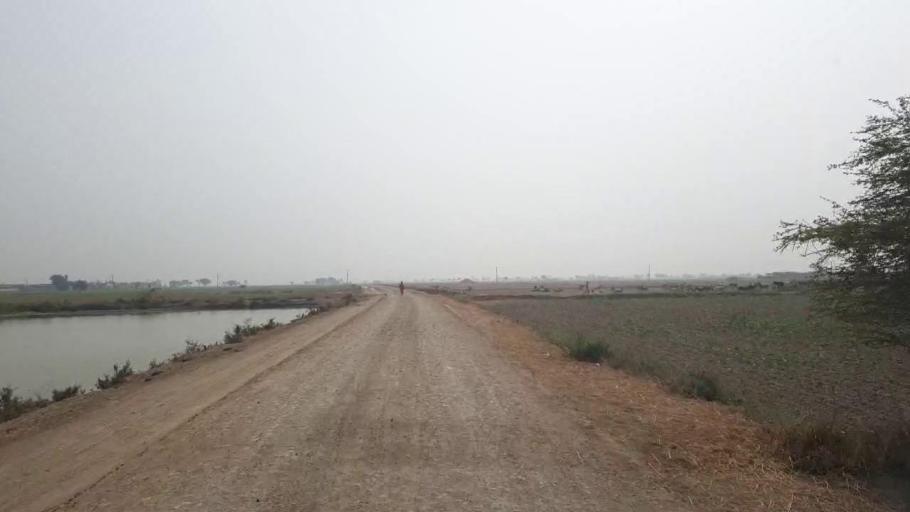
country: PK
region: Sindh
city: Kario
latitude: 24.6500
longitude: 68.5954
